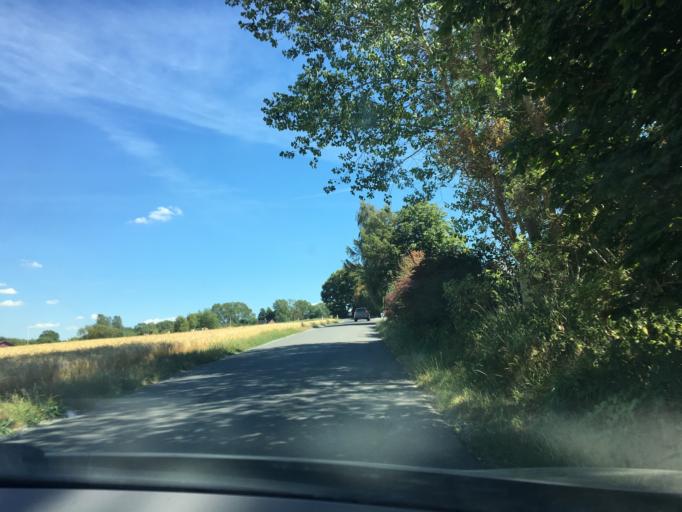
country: DK
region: South Denmark
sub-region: Middelfart Kommune
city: Norre Aby
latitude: 55.5063
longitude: 9.8755
